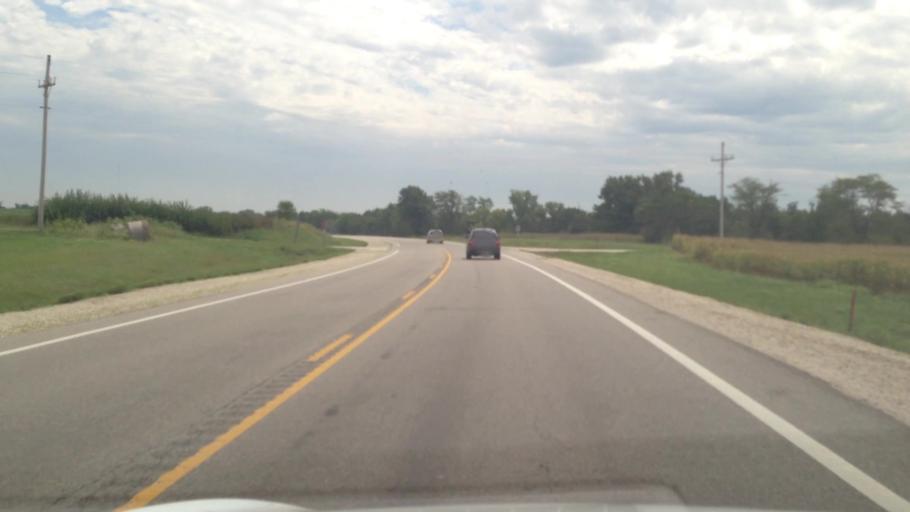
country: US
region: Kansas
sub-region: Allen County
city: Iola
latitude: 37.9163
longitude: -95.1527
